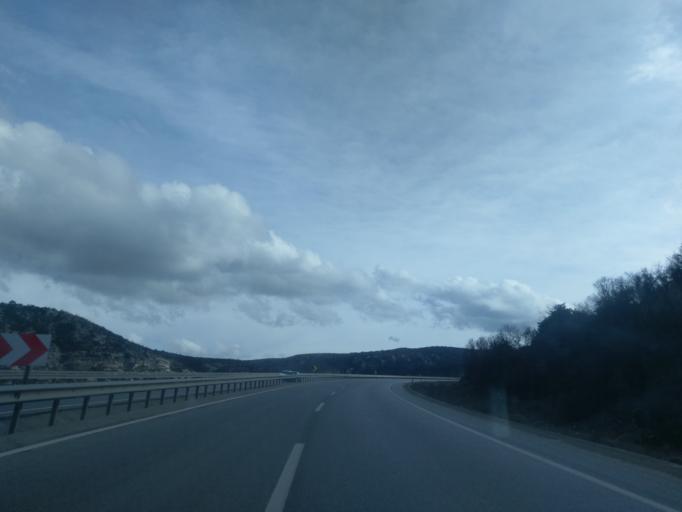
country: TR
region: Kuetahya
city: Sabuncu
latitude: 39.5627
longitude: 30.0755
